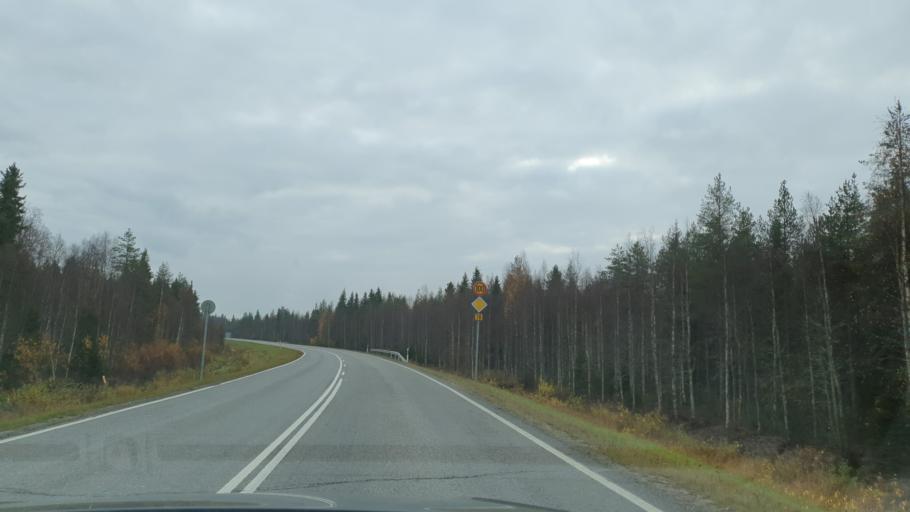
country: FI
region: Lapland
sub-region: Rovaniemi
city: Ranua
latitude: 66.0123
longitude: 26.3191
